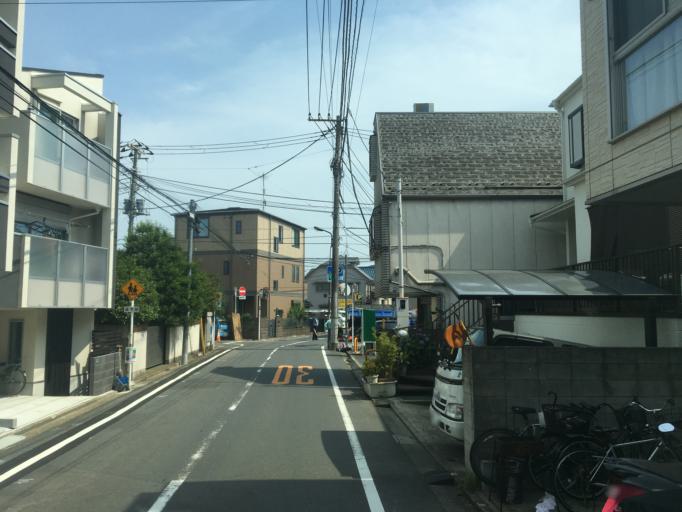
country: JP
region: Tokyo
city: Tokyo
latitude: 35.7422
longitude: 139.6932
